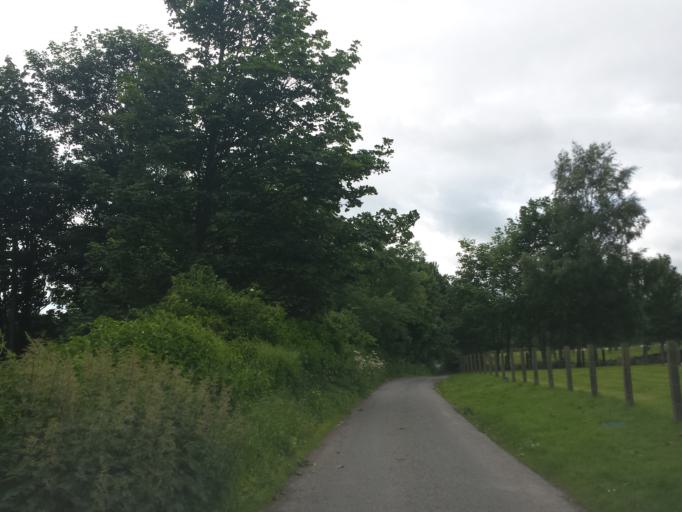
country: GB
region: Scotland
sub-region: Highland
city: Nairn
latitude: 57.5073
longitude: -4.0045
